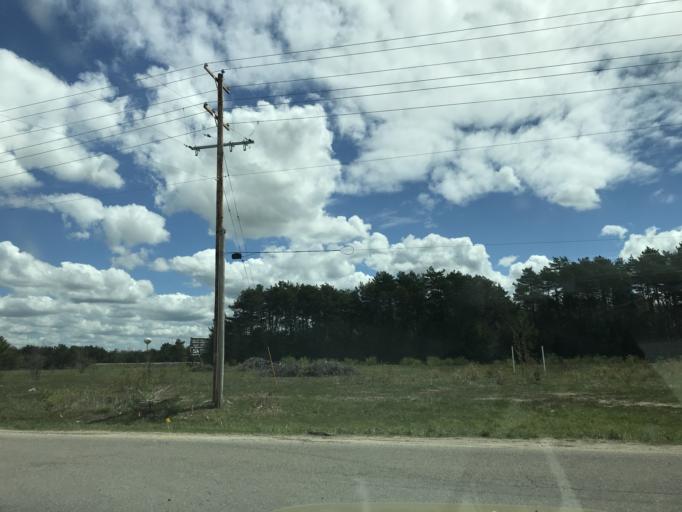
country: US
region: Michigan
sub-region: Otsego County
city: Gaylord
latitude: 45.0338
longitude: -84.6943
